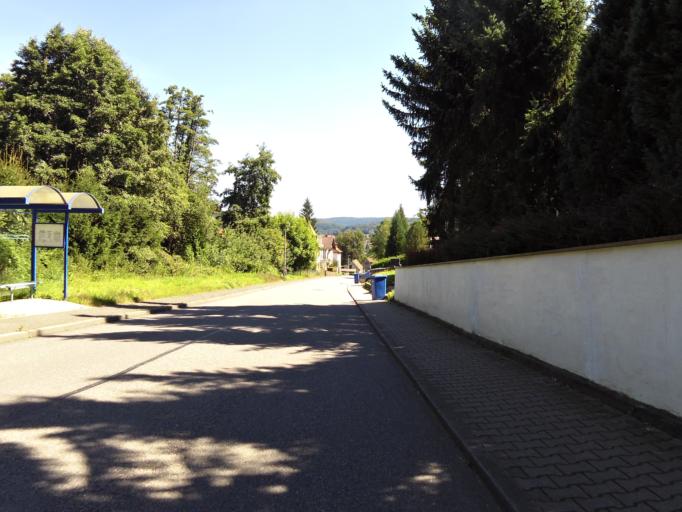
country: DE
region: Hesse
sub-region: Regierungsbezirk Darmstadt
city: Erbach
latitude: 49.6545
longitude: 8.9854
